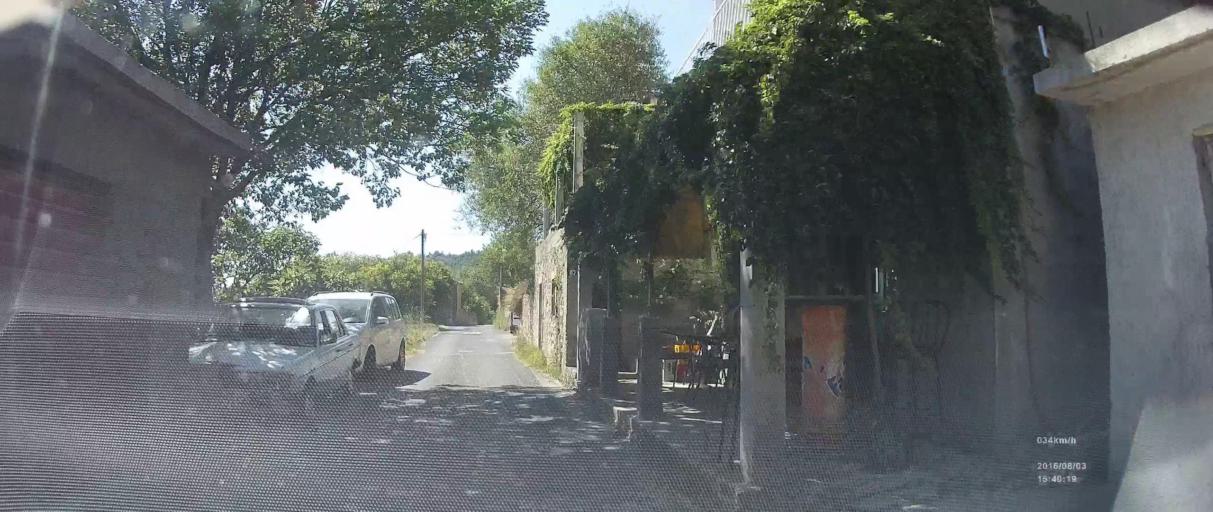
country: HR
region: Dubrovacko-Neretvanska
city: Blato
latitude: 42.7387
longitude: 17.5410
